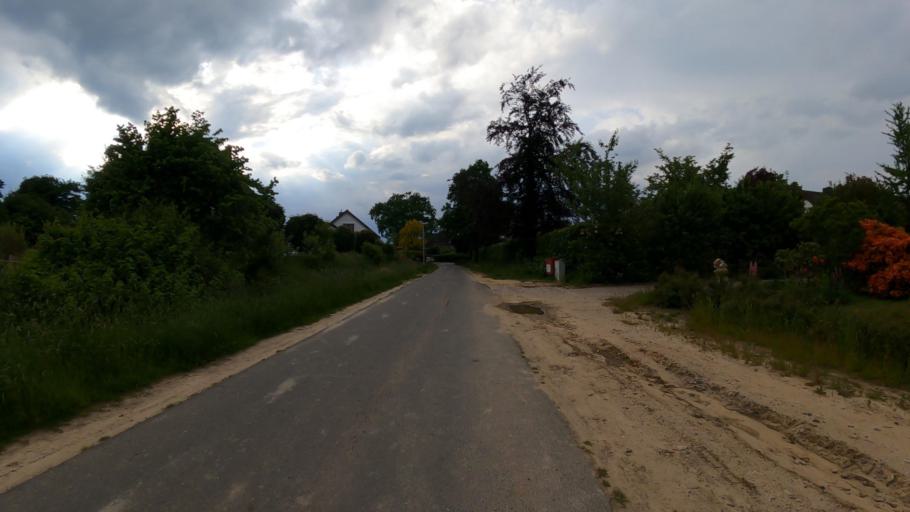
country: DE
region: Schleswig-Holstein
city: Appen
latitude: 53.6580
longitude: 9.7548
